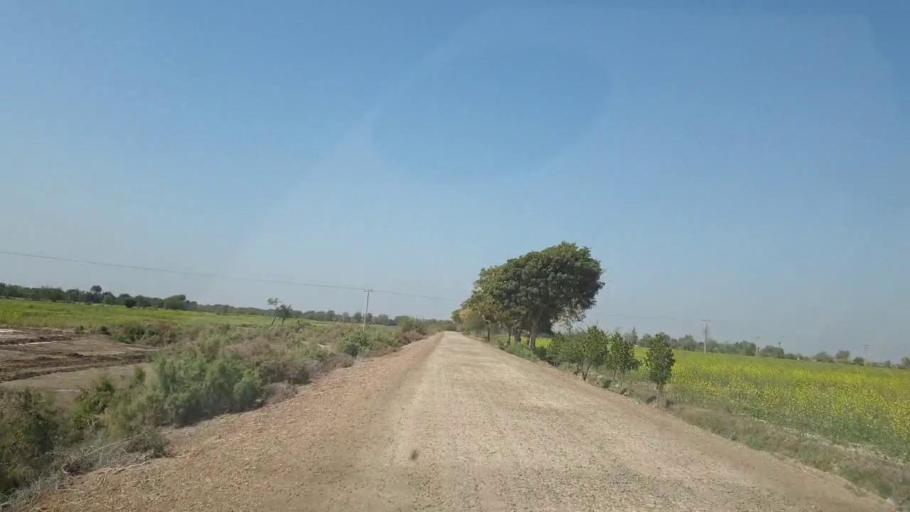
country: PK
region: Sindh
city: Mirpur Khas
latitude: 25.6968
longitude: 69.1020
